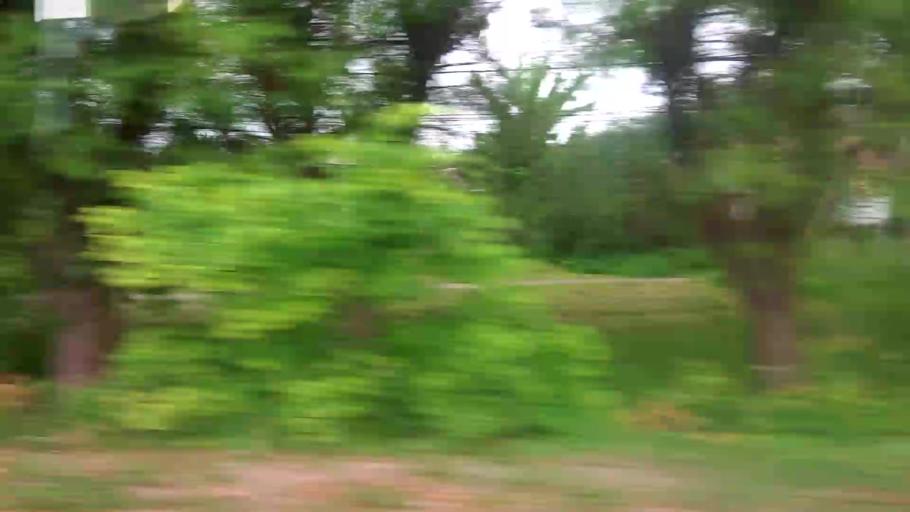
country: RU
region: Moskovskaya
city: Lukhovitsy
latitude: 54.9327
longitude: 39.0039
